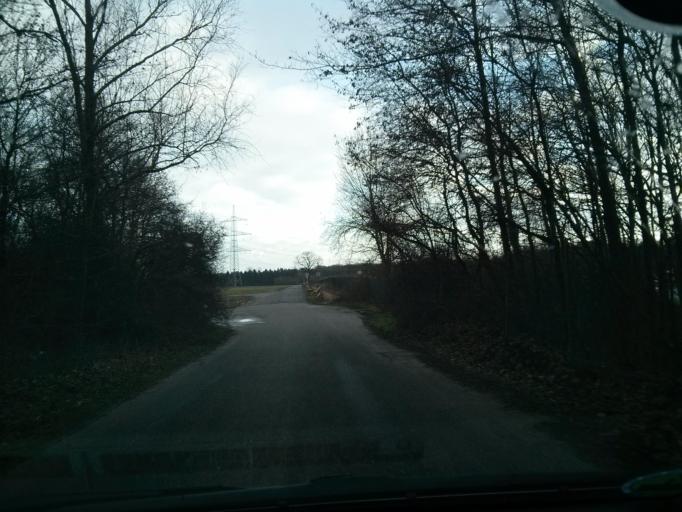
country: DE
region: North Rhine-Westphalia
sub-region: Regierungsbezirk Koln
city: Alfter
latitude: 50.6777
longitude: 7.0051
